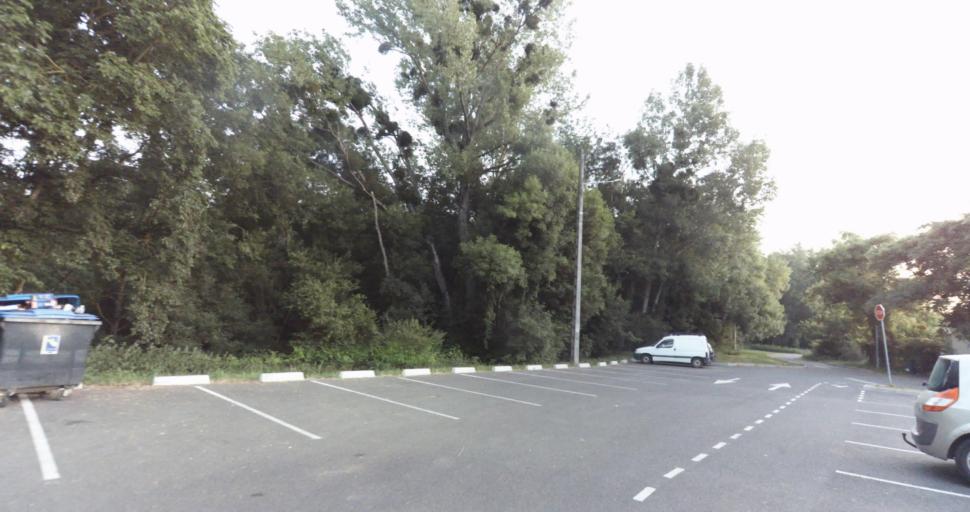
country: FR
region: Midi-Pyrenees
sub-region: Departement de la Haute-Garonne
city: Levignac
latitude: 43.6683
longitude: 1.1929
